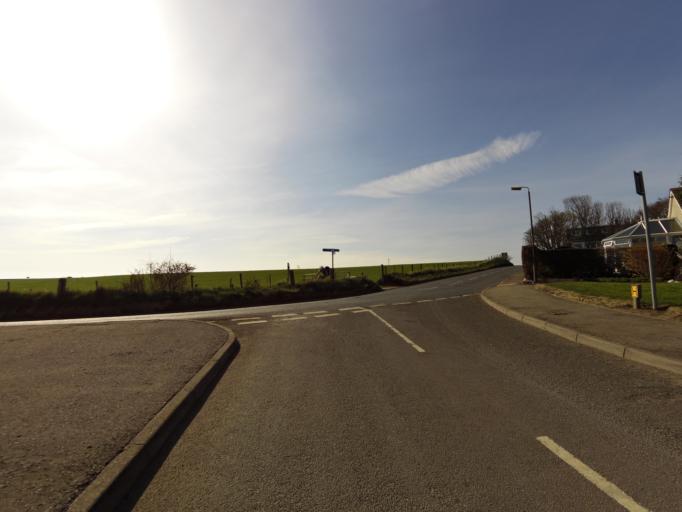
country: GB
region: Scotland
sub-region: Angus
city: Carnoustie
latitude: 56.5163
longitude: -2.6681
